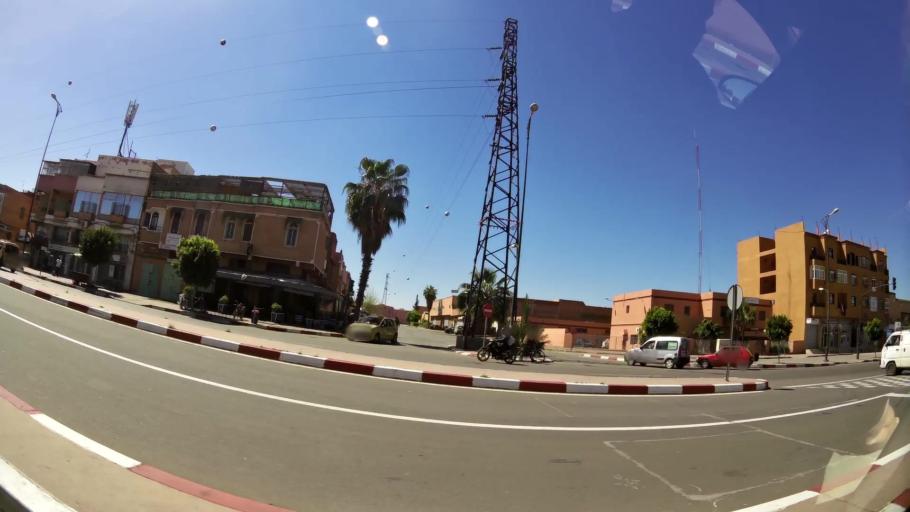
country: MA
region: Marrakech-Tensift-Al Haouz
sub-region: Marrakech
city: Marrakesh
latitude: 31.6276
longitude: -8.0388
